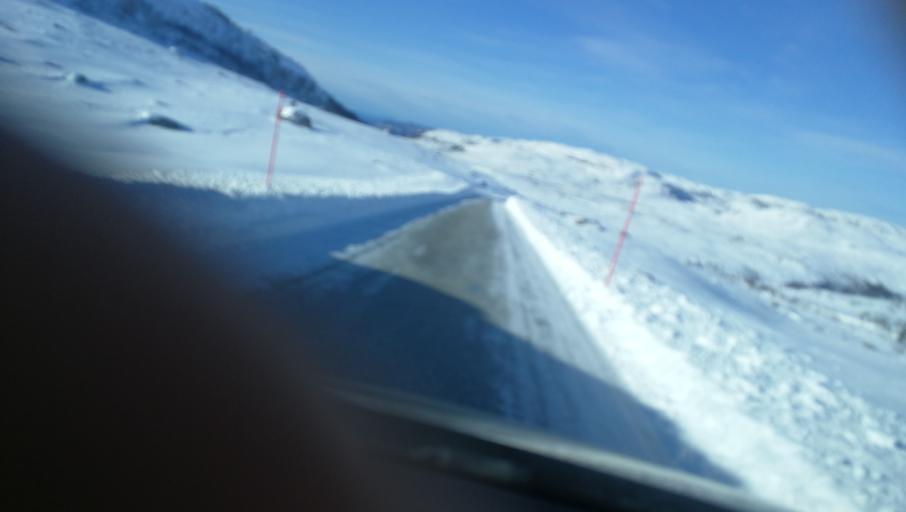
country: NO
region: Rogaland
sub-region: Hjelmeland
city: Hjelmelandsvagen
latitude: 59.1008
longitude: 6.3865
